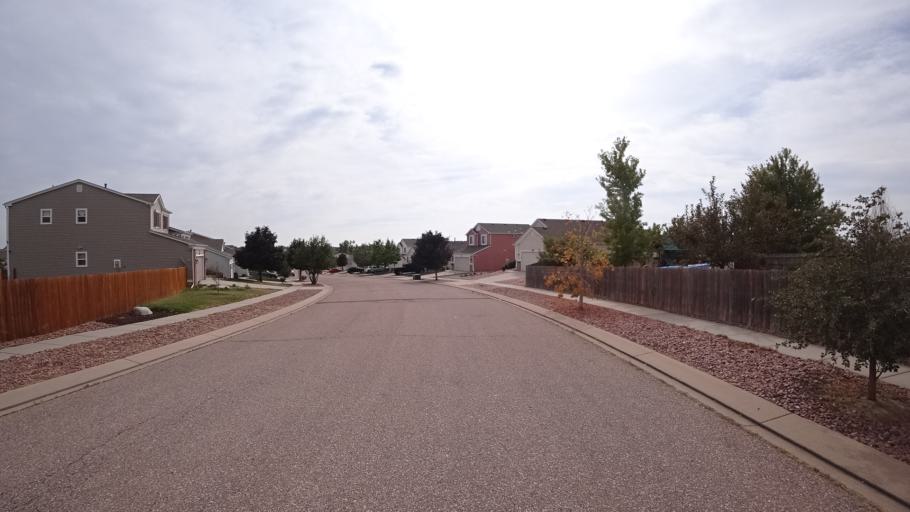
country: US
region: Colorado
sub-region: El Paso County
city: Cimarron Hills
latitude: 38.9152
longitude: -104.7052
